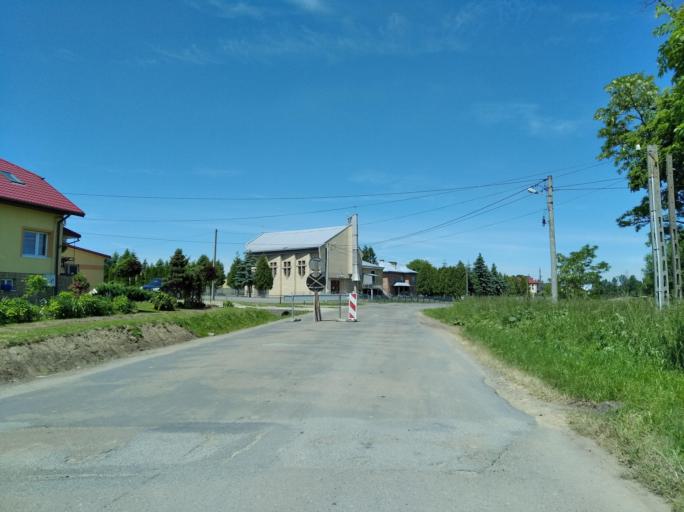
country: PL
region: Subcarpathian Voivodeship
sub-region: Powiat jasielski
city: Tarnowiec
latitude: 49.6992
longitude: 21.5533
